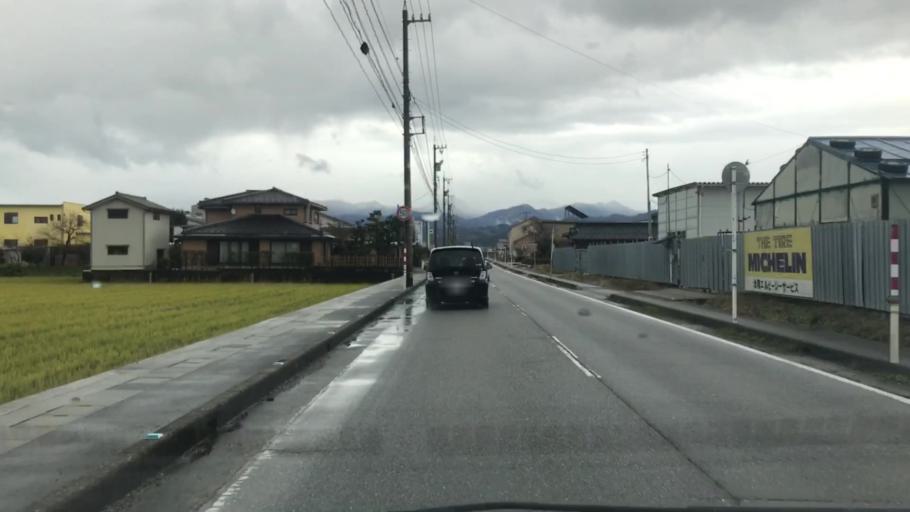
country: JP
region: Toyama
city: Kamiichi
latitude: 36.6859
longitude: 137.3271
